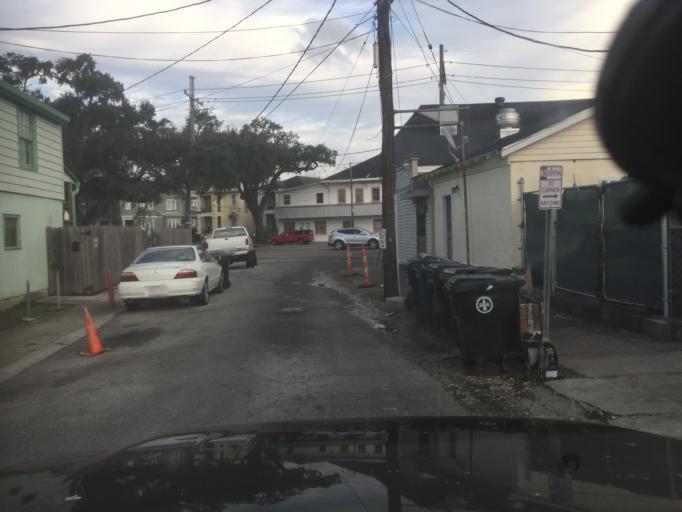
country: US
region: Louisiana
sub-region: Orleans Parish
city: New Orleans
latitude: 29.9865
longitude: -90.0767
